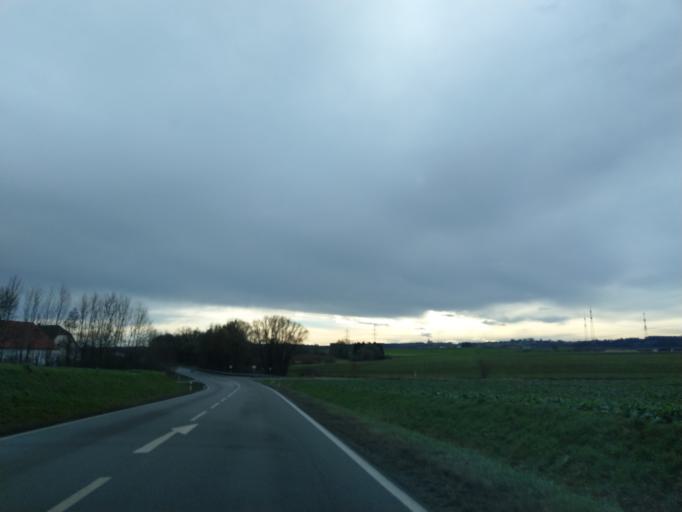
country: DE
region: Bavaria
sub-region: Lower Bavaria
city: Osterhofen
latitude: 48.6654
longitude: 13.0390
